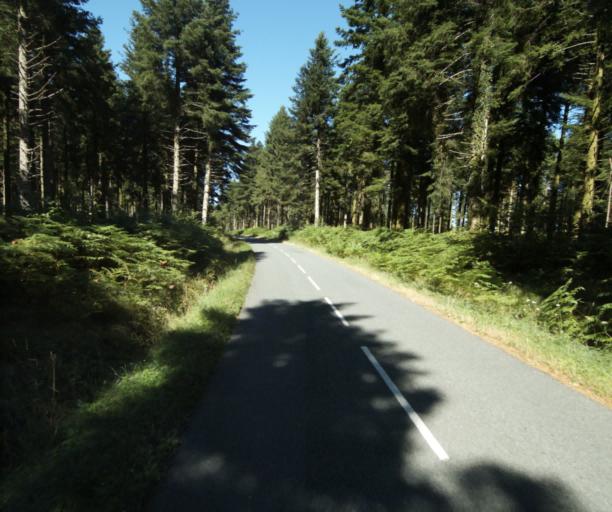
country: FR
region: Midi-Pyrenees
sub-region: Departement du Tarn
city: Dourgne
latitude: 43.4322
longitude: 2.1259
